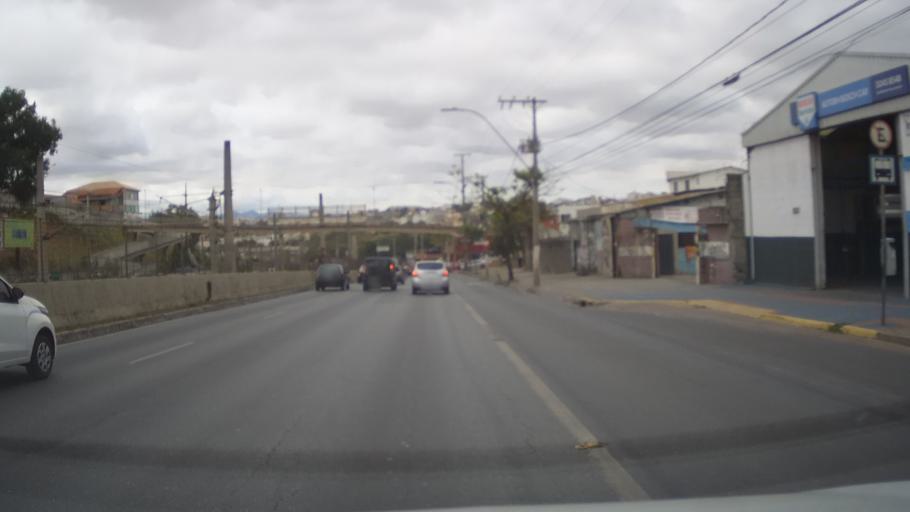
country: BR
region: Minas Gerais
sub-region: Belo Horizonte
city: Belo Horizonte
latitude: -19.8512
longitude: -43.9341
